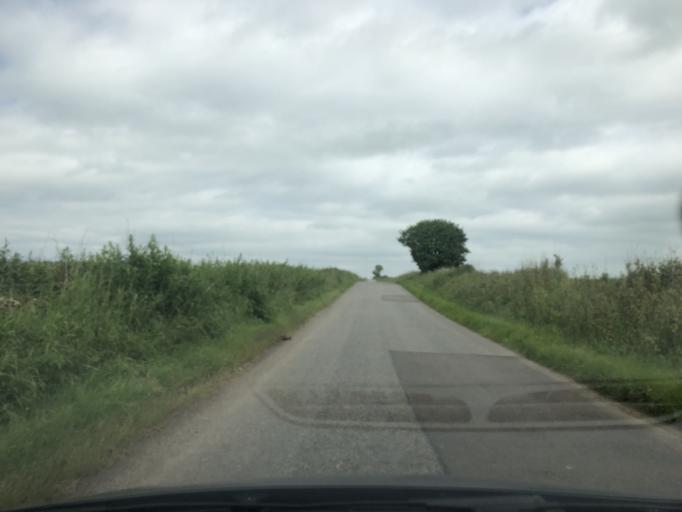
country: GB
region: Scotland
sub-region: Angus
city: Forfar
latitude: 56.7252
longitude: -2.9137
